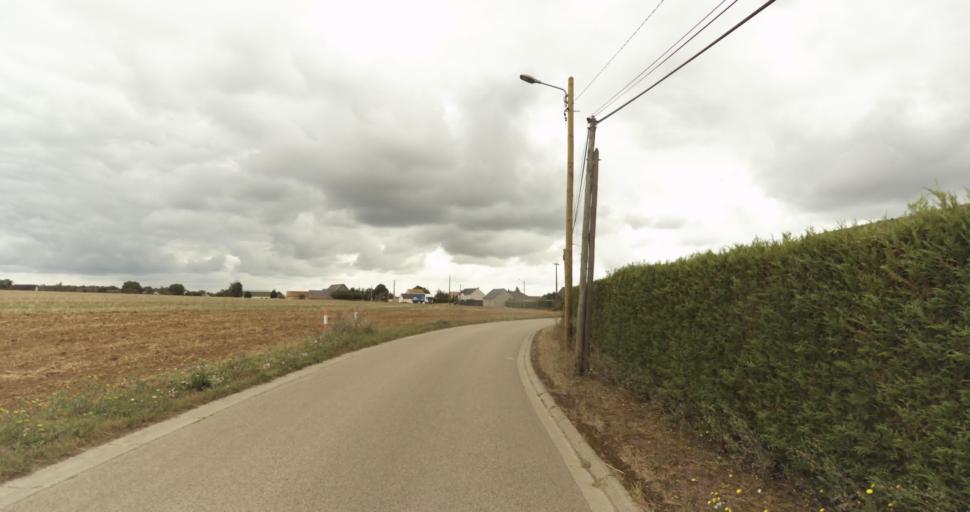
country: FR
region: Haute-Normandie
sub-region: Departement de l'Eure
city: Menilles
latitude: 49.0226
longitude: 1.3033
